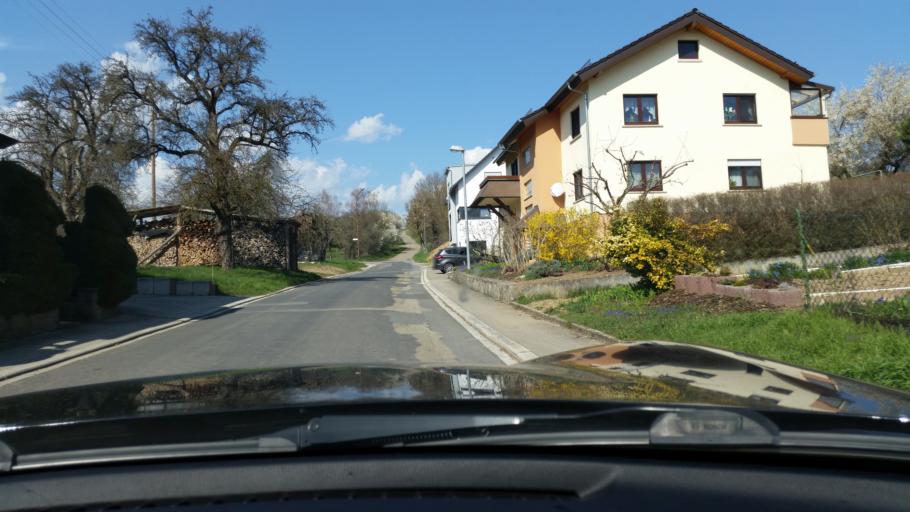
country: DE
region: Baden-Wuerttemberg
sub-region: Regierungsbezirk Stuttgart
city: Krautheim
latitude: 49.3713
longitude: 9.6149
